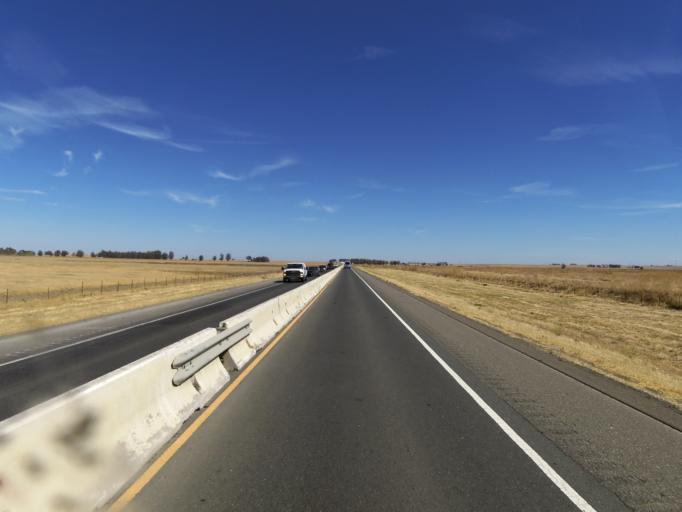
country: US
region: California
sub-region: Solano County
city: Suisun
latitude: 38.2284
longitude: -121.9272
